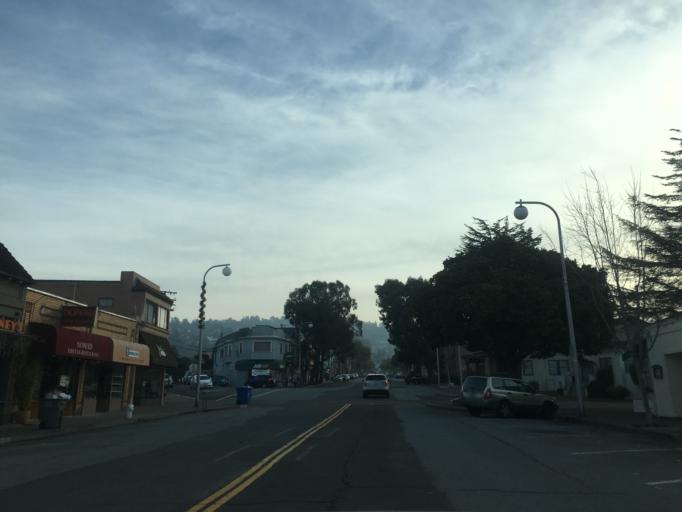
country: US
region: California
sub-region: Alameda County
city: Albany
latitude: 37.8911
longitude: -122.2851
